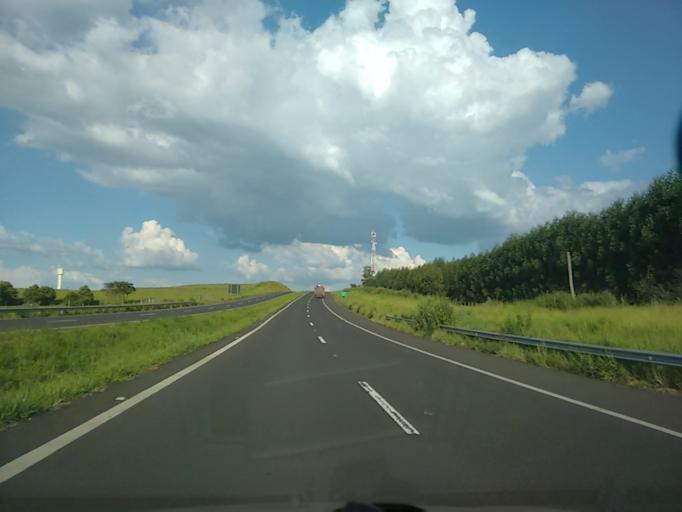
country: BR
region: Sao Paulo
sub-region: Duartina
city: Duartina
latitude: -22.3249
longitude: -49.4237
